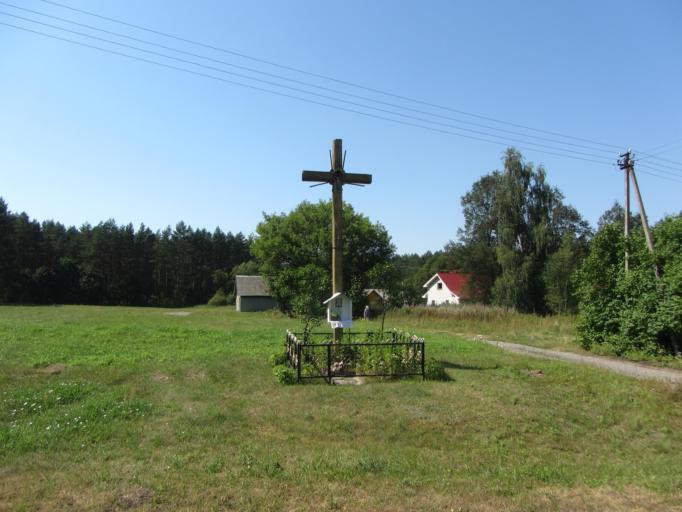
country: LT
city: Skaidiskes
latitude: 54.6076
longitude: 25.5396
